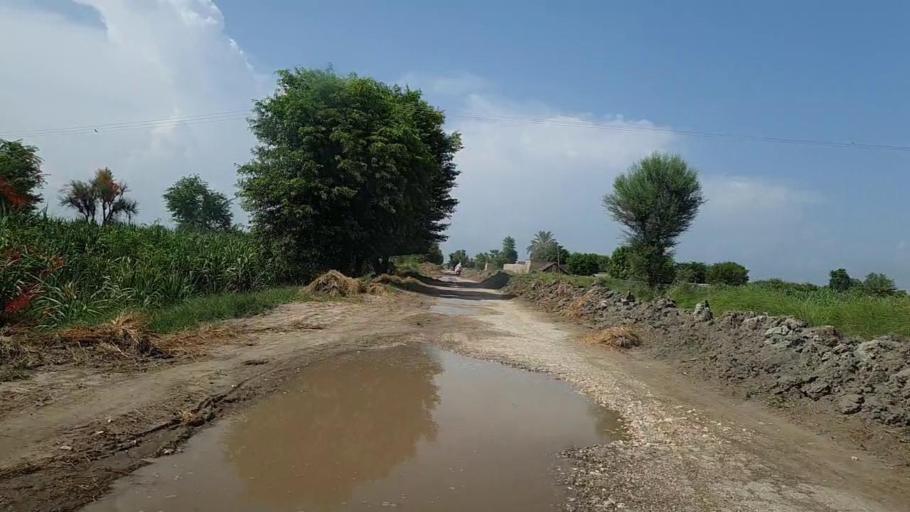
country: PK
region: Sindh
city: Bhiria
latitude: 26.8908
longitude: 68.2370
